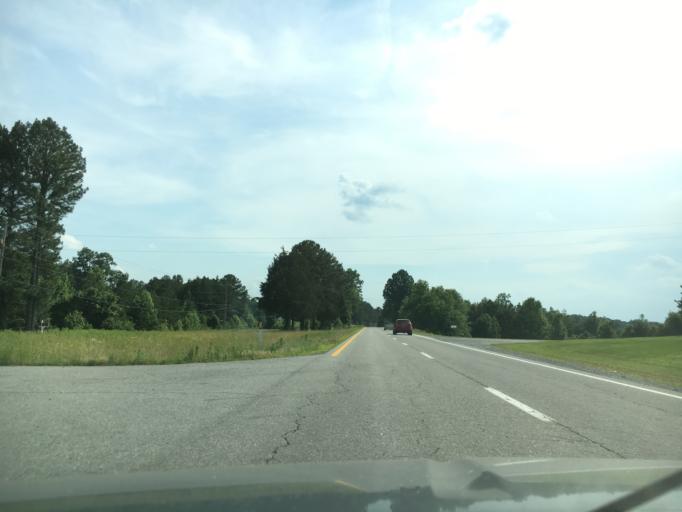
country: US
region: Virginia
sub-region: Halifax County
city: Halifax
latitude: 36.7882
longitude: -78.8019
